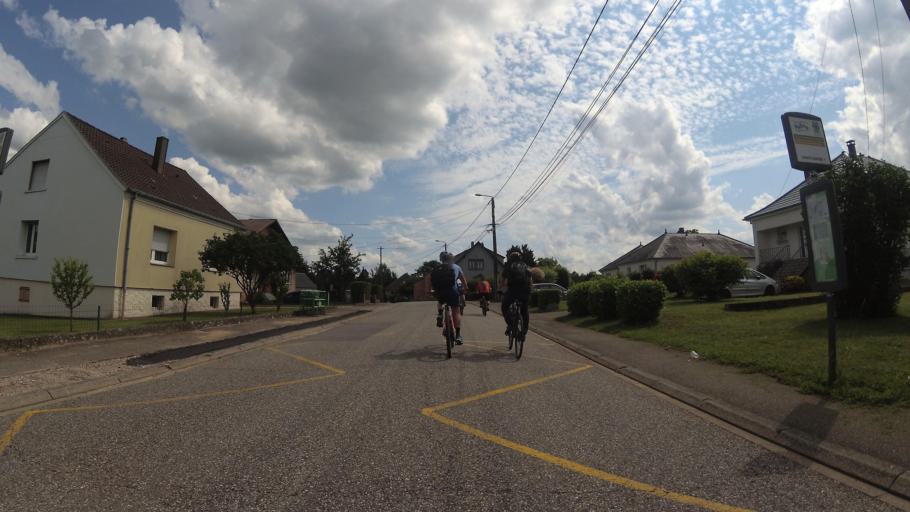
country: FR
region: Lorraine
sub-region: Departement de la Moselle
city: Sarreinsming
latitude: 49.1220
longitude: 7.1207
